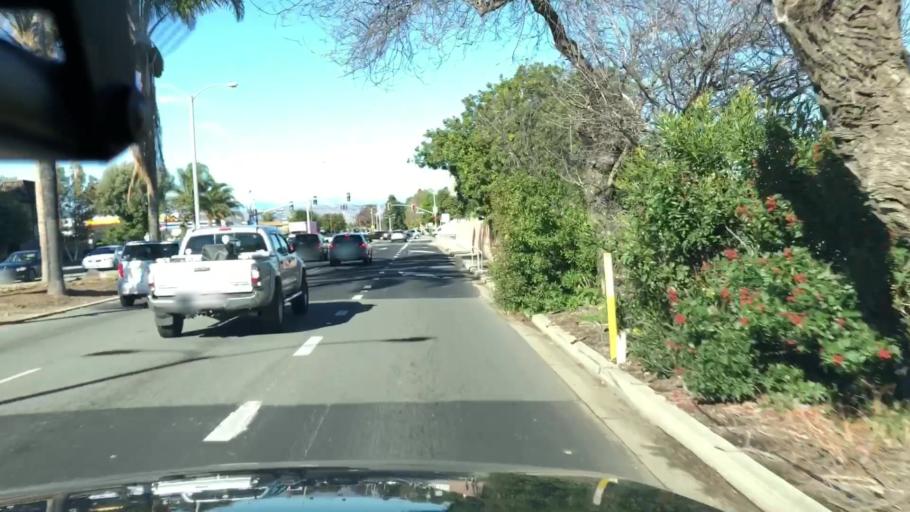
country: US
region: California
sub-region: Ventura County
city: Oxnard
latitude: 34.2180
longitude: -119.1945
